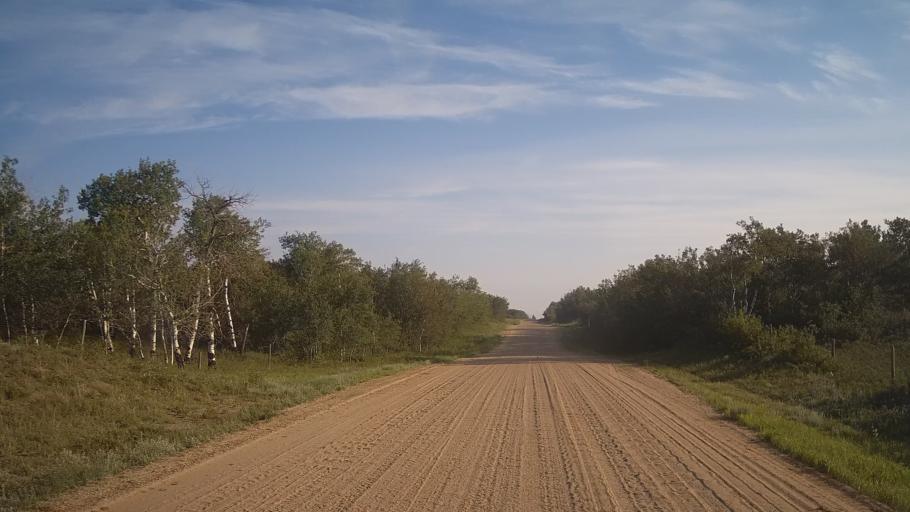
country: CA
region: Saskatchewan
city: Saskatoon
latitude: 51.8366
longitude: -106.5239
